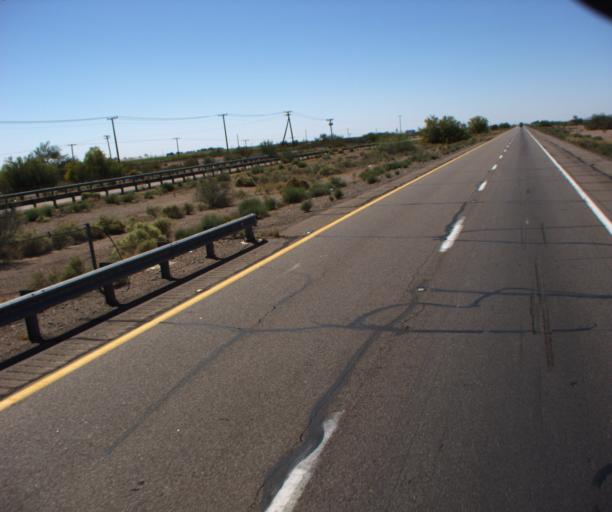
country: US
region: Arizona
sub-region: Maricopa County
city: Gila Bend
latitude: 32.9369
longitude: -112.7732
